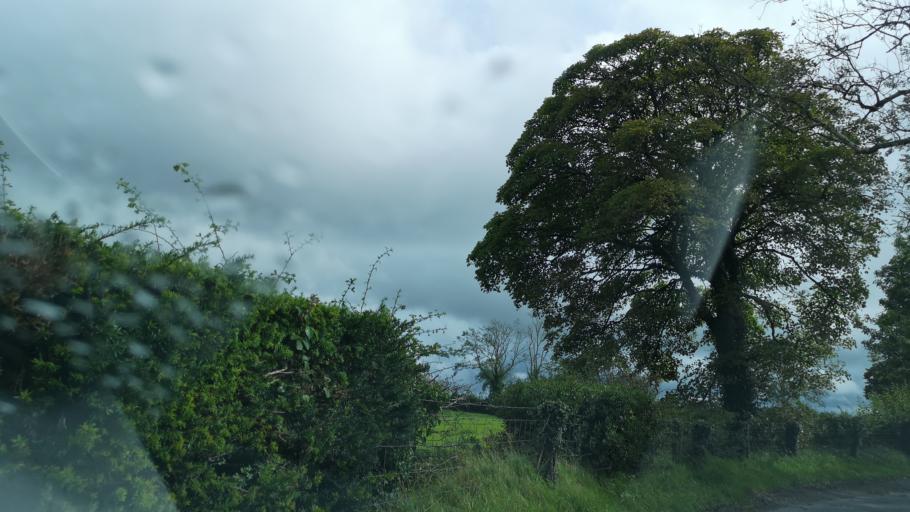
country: IE
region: Connaught
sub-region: County Galway
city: Loughrea
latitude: 53.3068
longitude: -8.5967
